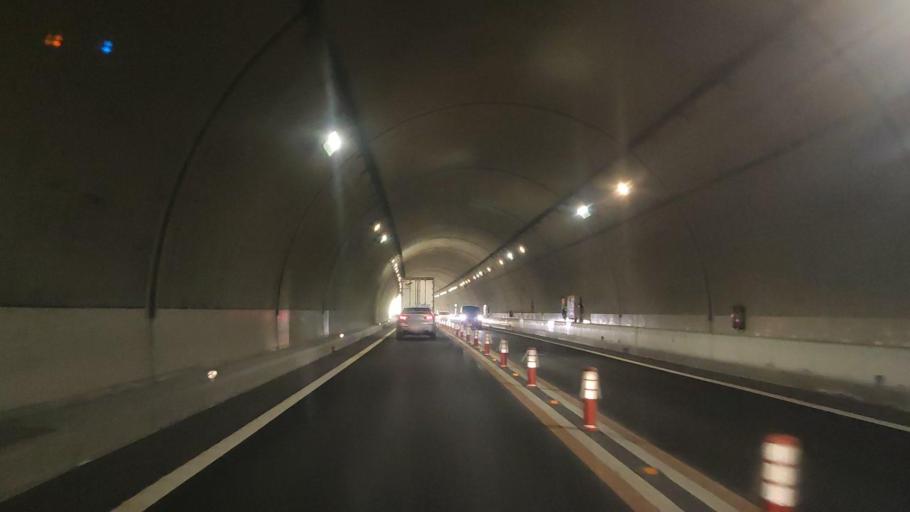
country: JP
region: Fukuoka
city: Kanda
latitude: 33.7887
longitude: 130.9705
